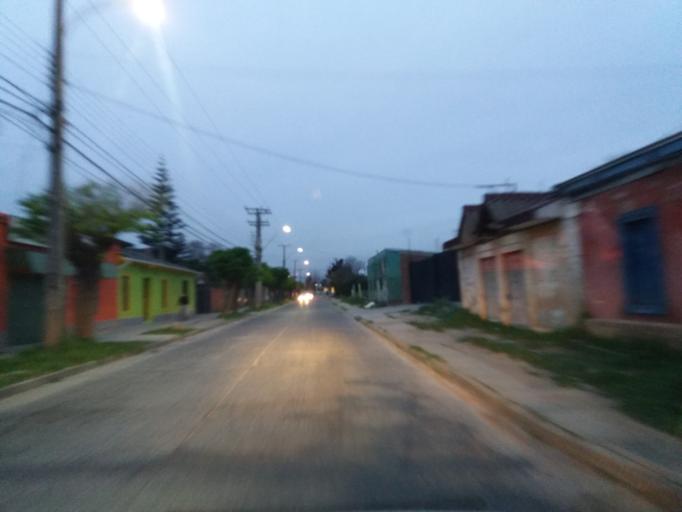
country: CL
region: Valparaiso
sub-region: Provincia de Marga Marga
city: Limache
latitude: -33.0055
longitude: -71.2644
